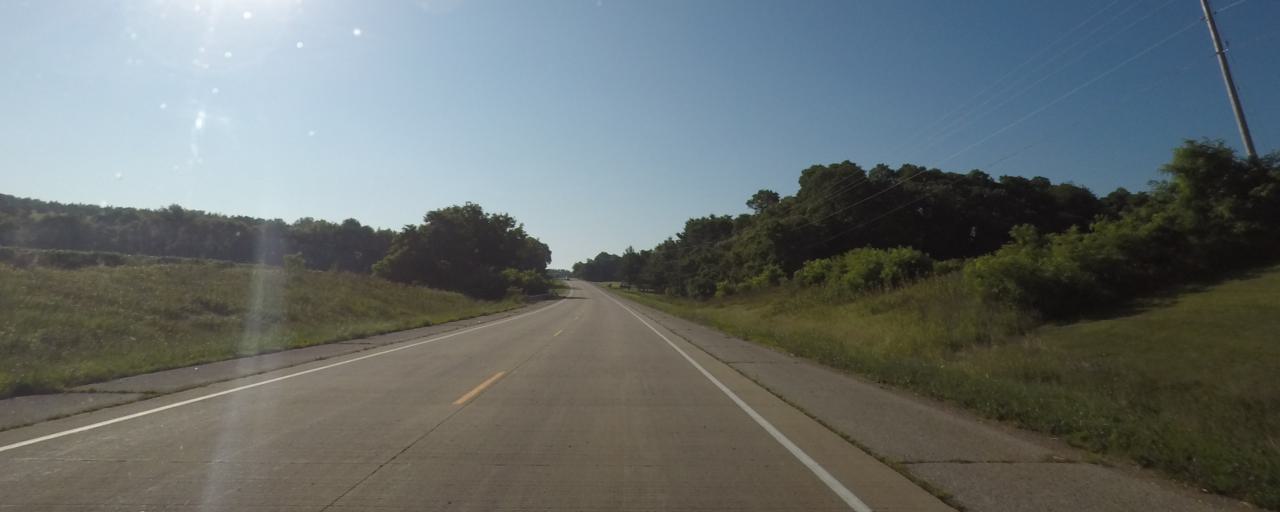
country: US
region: Wisconsin
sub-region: Jefferson County
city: Lake Koshkonong
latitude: 42.9671
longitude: -88.9091
